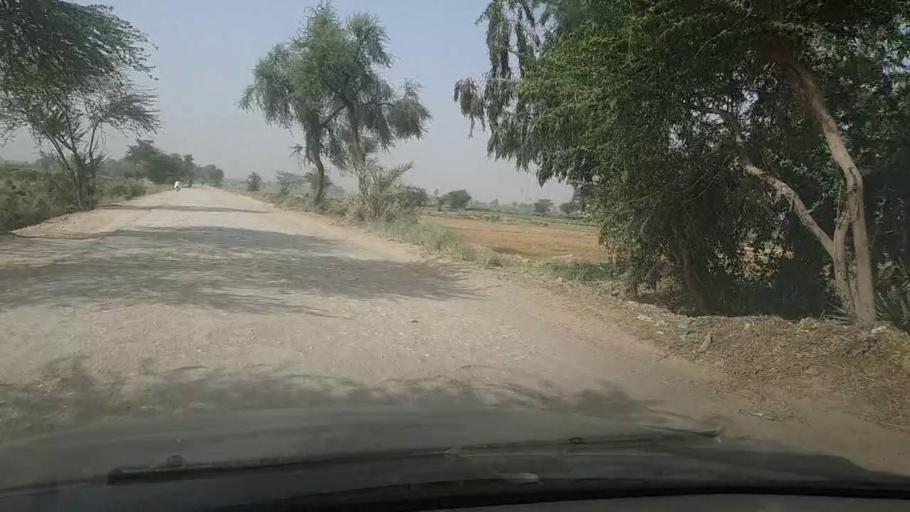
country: PK
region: Sindh
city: Shikarpur
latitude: 27.9283
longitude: 68.6161
